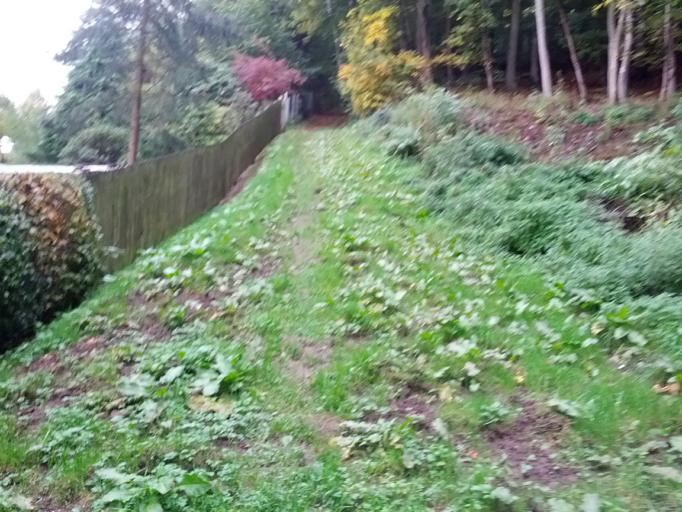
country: DE
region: Thuringia
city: Eisenach
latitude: 50.9756
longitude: 10.2955
